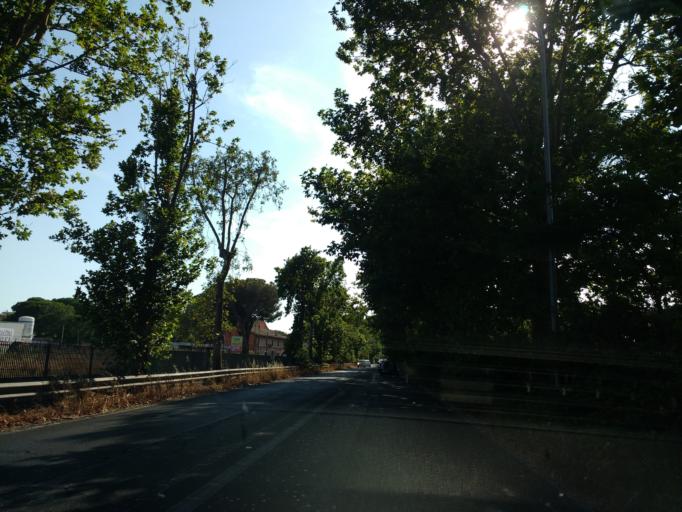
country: IT
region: Latium
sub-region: Citta metropolitana di Roma Capitale
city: Vitinia
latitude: 41.7933
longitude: 12.3905
